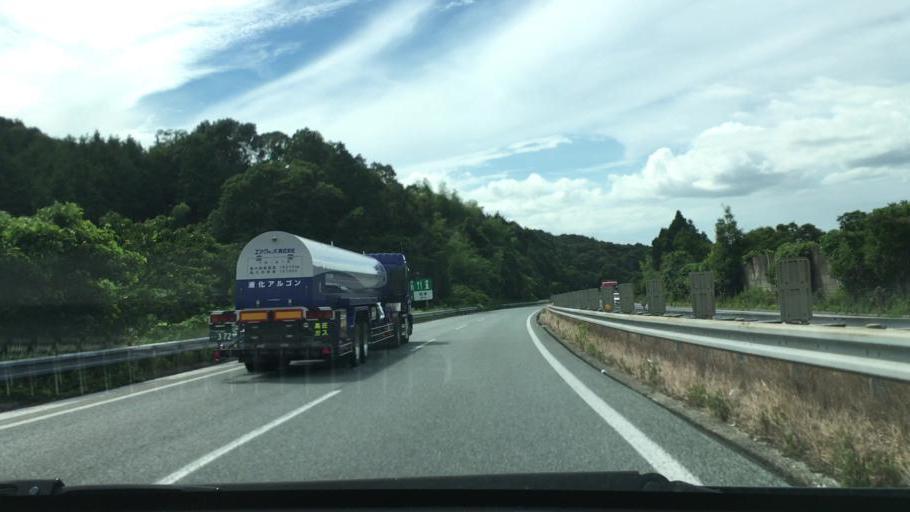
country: JP
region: Yamaguchi
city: Ogori-shimogo
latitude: 34.1448
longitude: 131.3484
